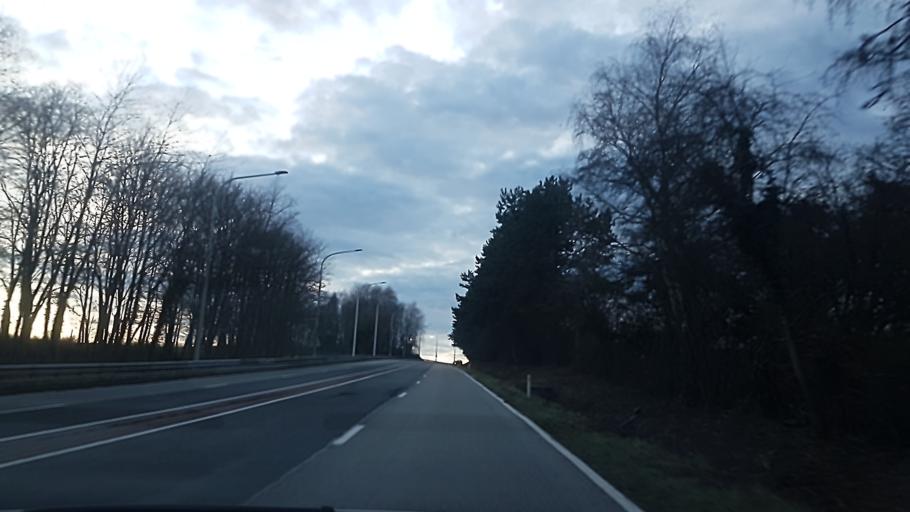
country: BE
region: Wallonia
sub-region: Province du Hainaut
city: Chimay
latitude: 50.0377
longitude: 4.3879
